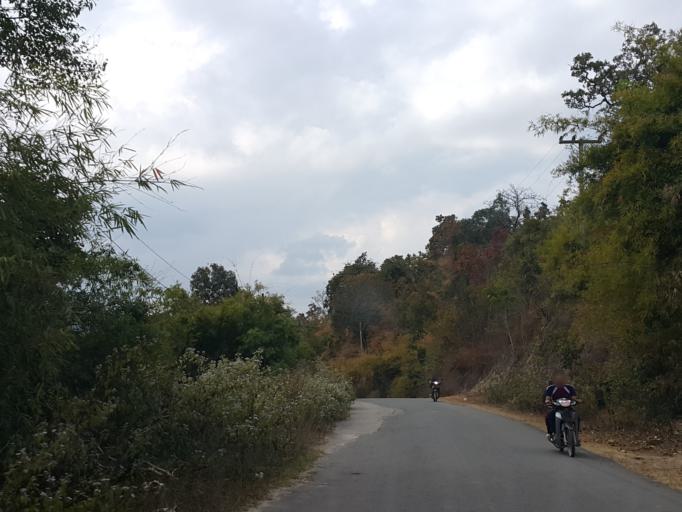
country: TH
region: Chiang Mai
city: Om Koi
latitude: 17.7980
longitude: 98.3457
